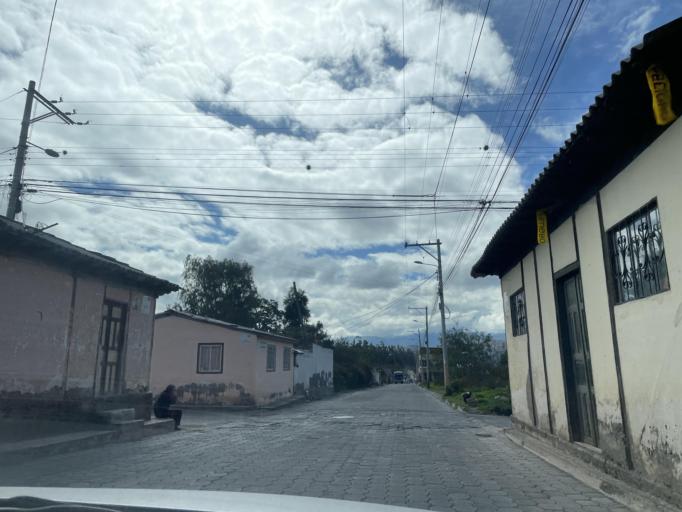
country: EC
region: Chimborazo
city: Guano
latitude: -1.6071
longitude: -78.6272
